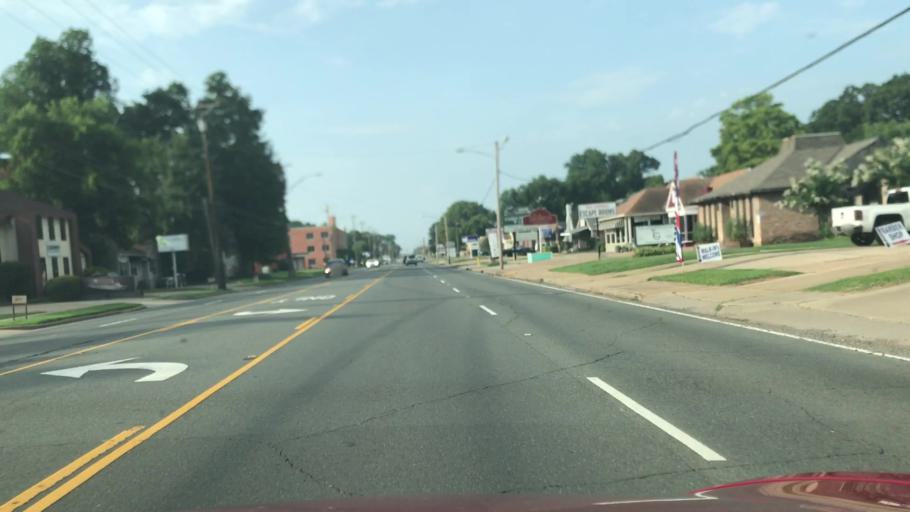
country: US
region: Louisiana
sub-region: Bossier Parish
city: Bossier City
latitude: 32.4741
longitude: -93.7222
